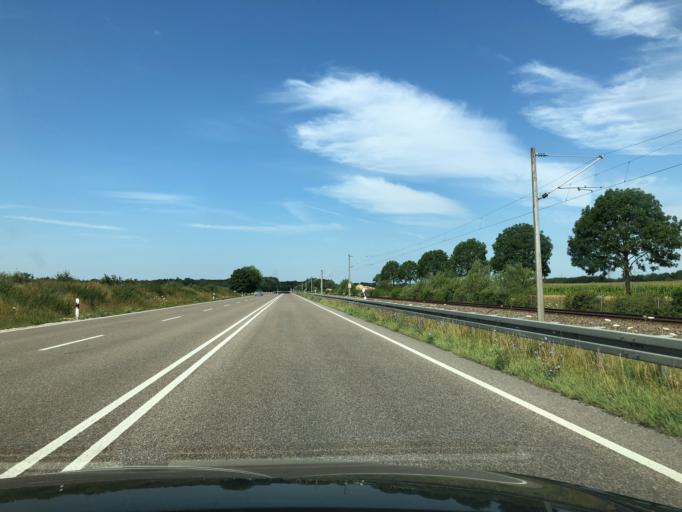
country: DE
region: Bavaria
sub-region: Upper Bavaria
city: Karlskron
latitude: 48.7057
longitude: 11.3870
